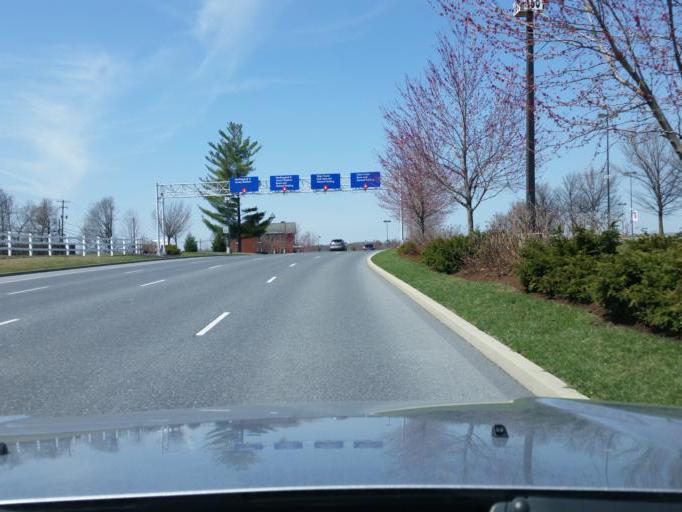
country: US
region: Pennsylvania
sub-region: Dauphin County
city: Hershey
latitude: 40.2837
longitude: -76.6724
